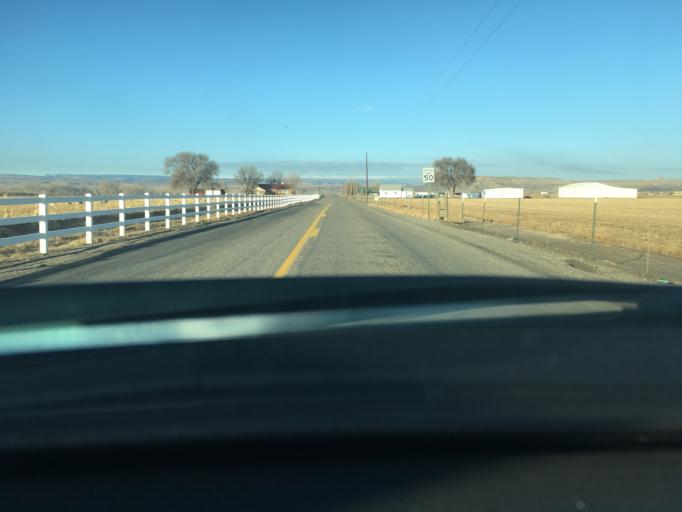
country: US
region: Colorado
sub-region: Delta County
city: Delta
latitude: 38.7483
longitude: -108.1310
